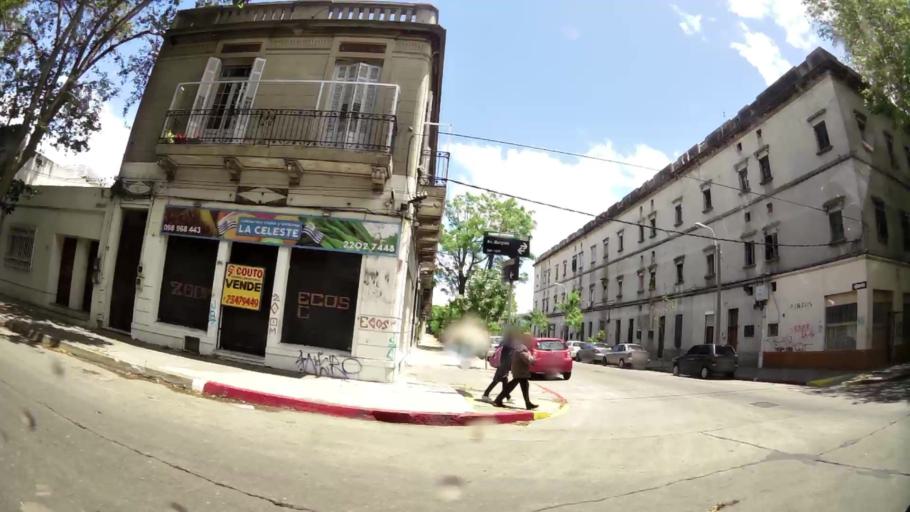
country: UY
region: Montevideo
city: Montevideo
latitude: -34.8721
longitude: -56.1859
